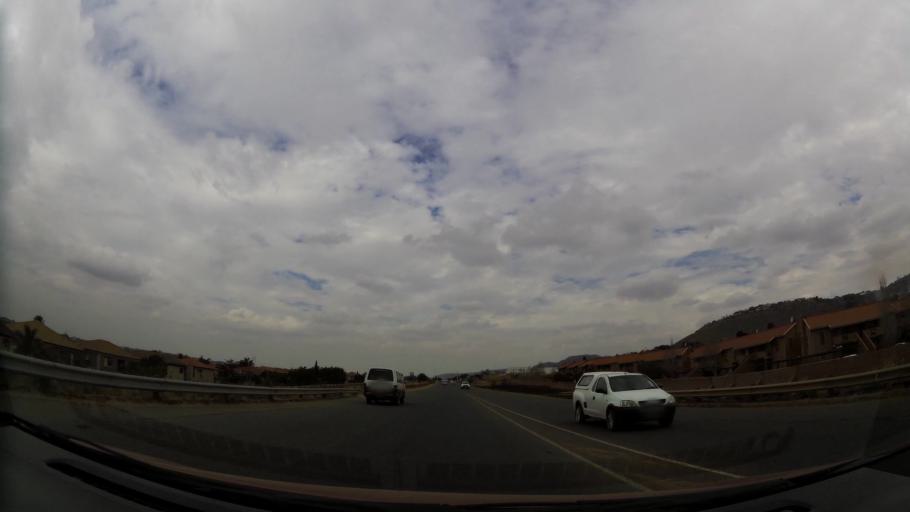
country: ZA
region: Gauteng
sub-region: West Rand District Municipality
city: Muldersdriseloop
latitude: -26.0943
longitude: 27.8722
